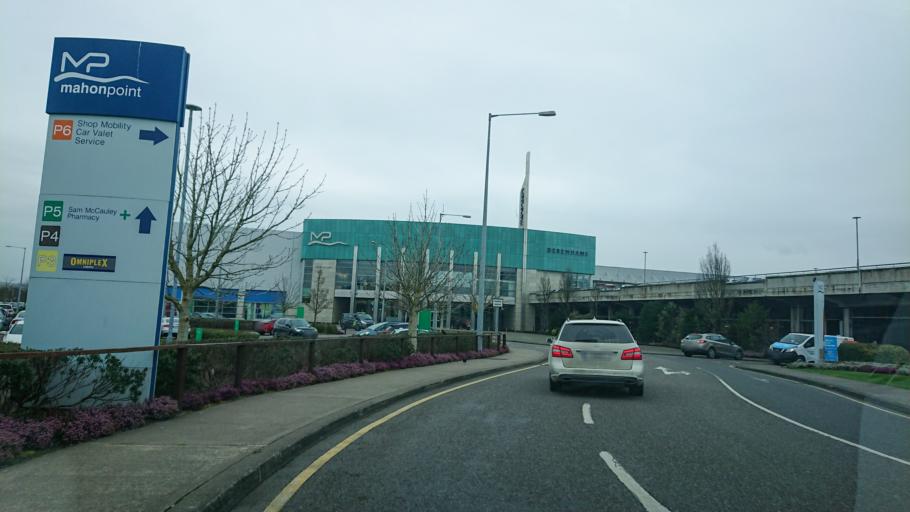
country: IE
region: Munster
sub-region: County Cork
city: Passage West
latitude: 51.8856
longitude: -8.3988
